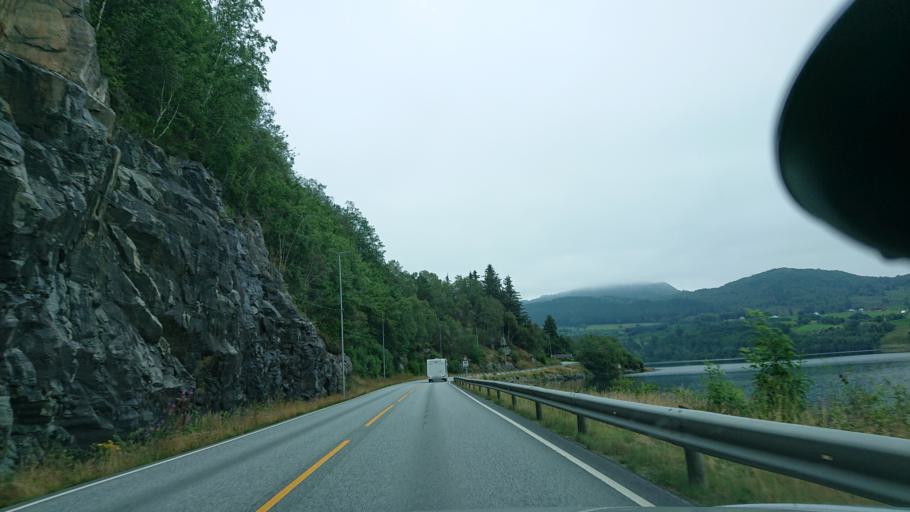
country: NO
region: Rogaland
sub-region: Strand
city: Tau
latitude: 59.0687
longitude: 5.9594
